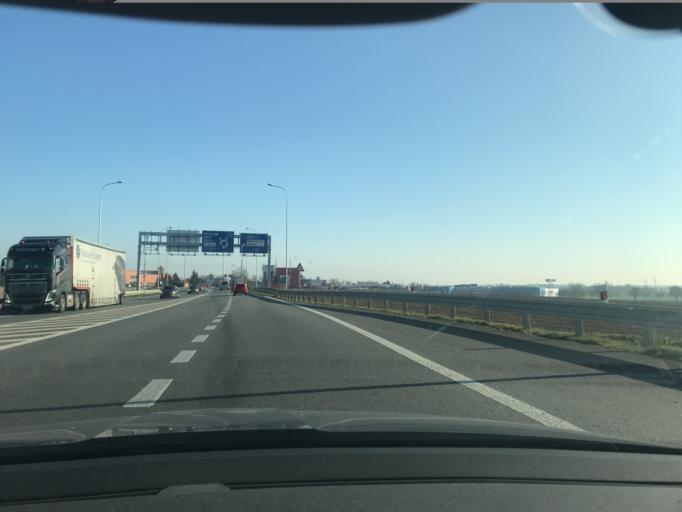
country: CZ
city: Stezery
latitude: 50.2014
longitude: 15.7706
